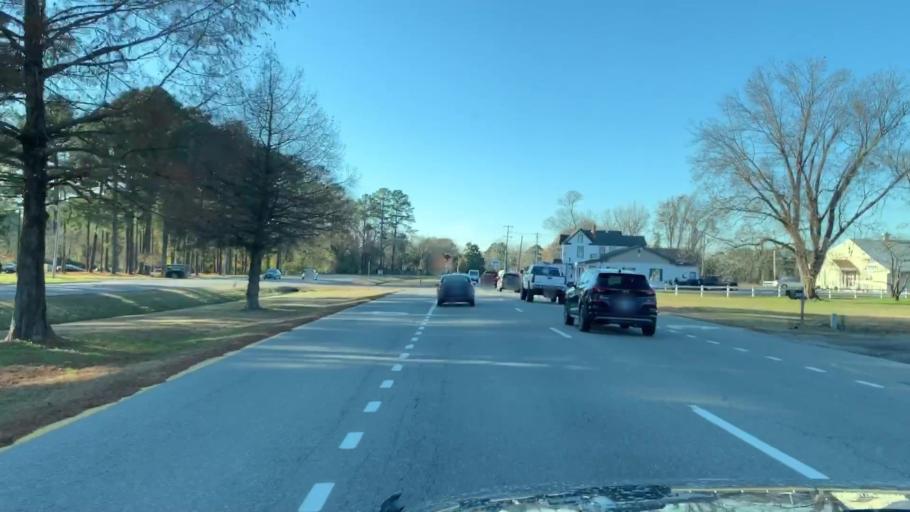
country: US
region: Virginia
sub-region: James City County
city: Williamsburg
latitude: 37.3776
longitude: -76.7989
